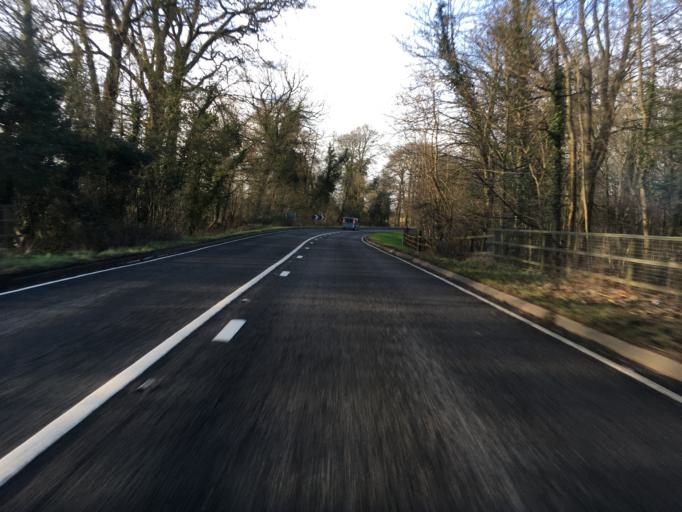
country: GB
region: England
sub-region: Warwickshire
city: Henley in Arden
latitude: 52.2494
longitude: -1.7547
